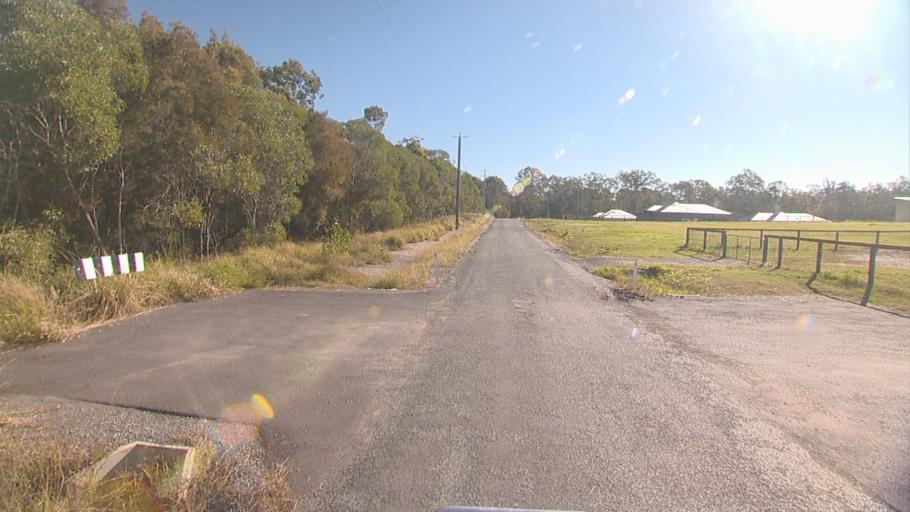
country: AU
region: Queensland
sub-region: Logan
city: Logan Reserve
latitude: -27.7544
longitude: 153.1414
